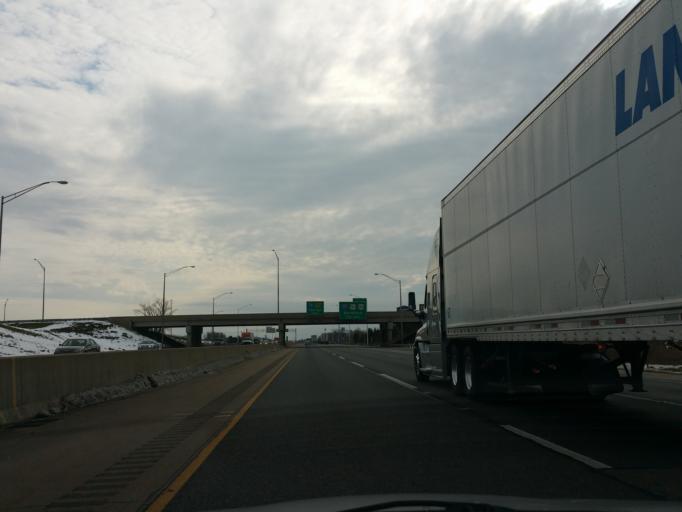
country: US
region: Illinois
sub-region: Winnebago County
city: Cherry Valley
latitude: 42.2770
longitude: -88.9649
